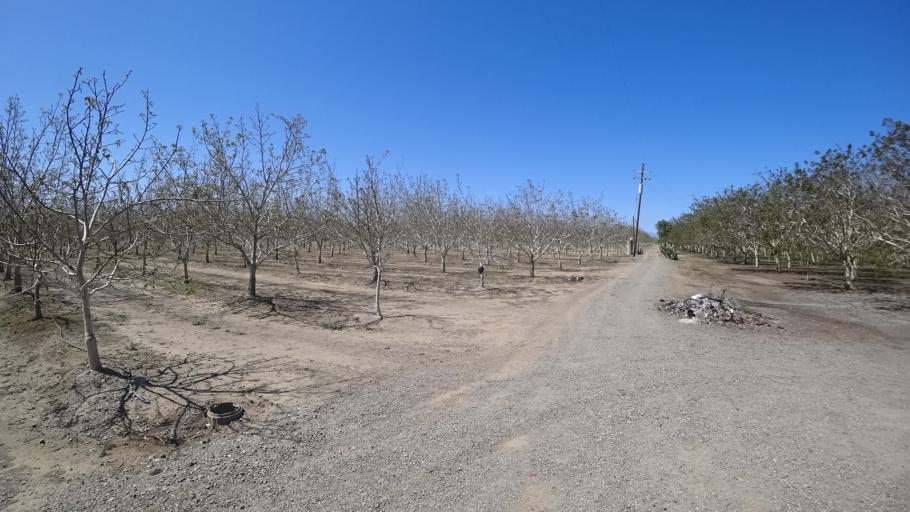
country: US
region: California
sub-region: Glenn County
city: Orland
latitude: 39.7035
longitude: -122.1454
